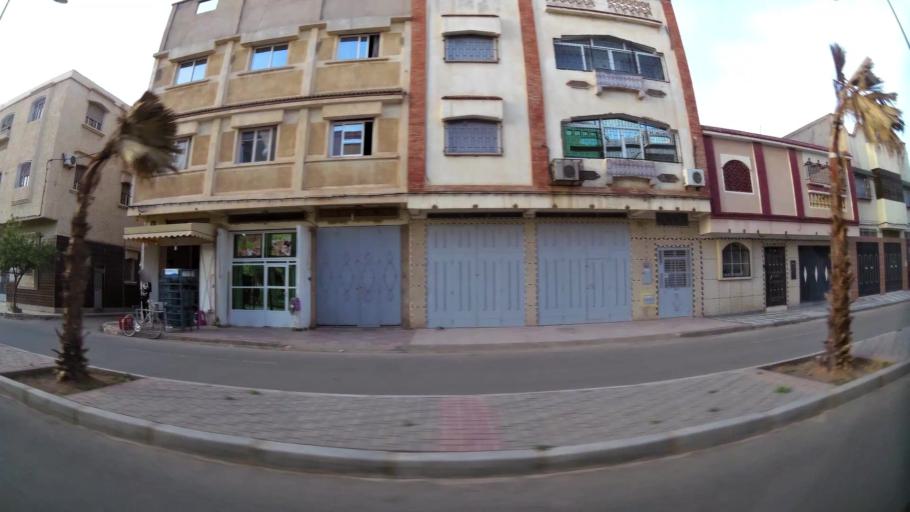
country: MA
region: Oriental
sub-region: Oujda-Angad
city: Oujda
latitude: 34.6781
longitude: -1.8825
